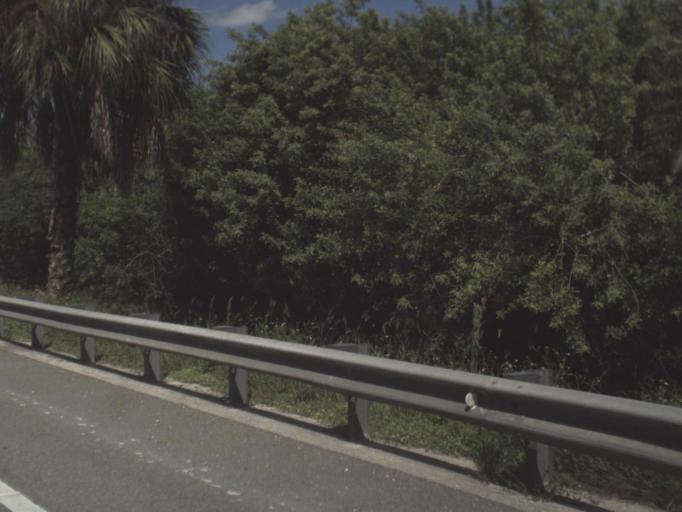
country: US
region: Florida
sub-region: Collier County
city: Lely Resort
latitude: 26.0277
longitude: -81.6434
